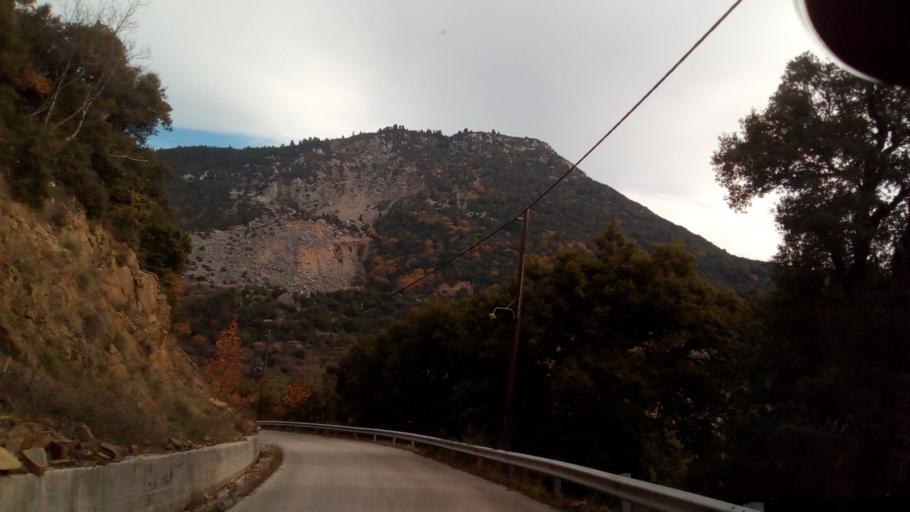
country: GR
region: West Greece
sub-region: Nomos Aitolias kai Akarnanias
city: Thermo
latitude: 38.6828
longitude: 21.9023
